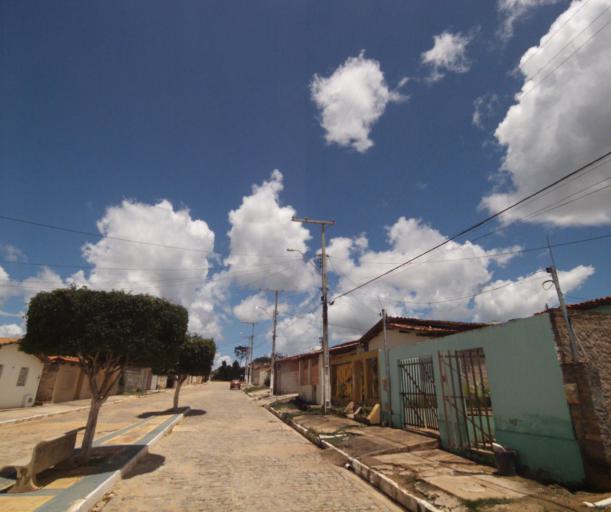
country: BR
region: Bahia
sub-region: Pocoes
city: Pocoes
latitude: -14.3753
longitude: -40.5008
